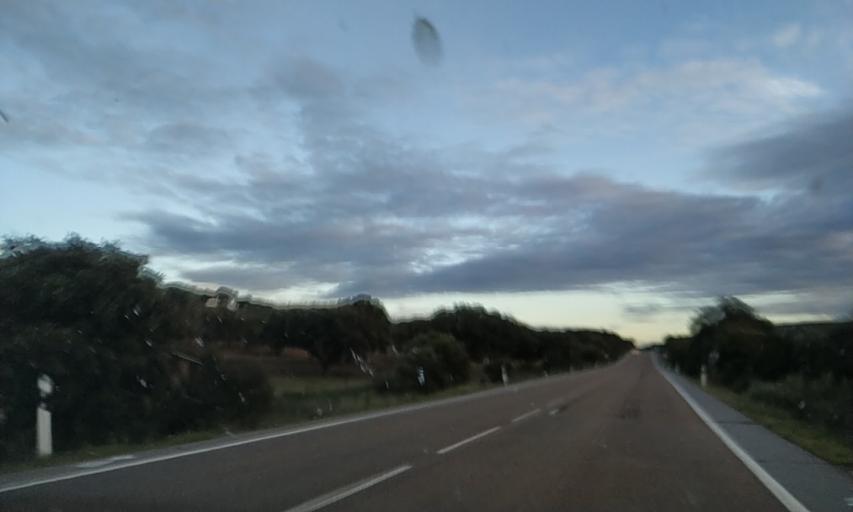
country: ES
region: Extremadura
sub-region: Provincia de Badajoz
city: Puebla de Obando
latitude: 39.2884
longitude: -6.5223
